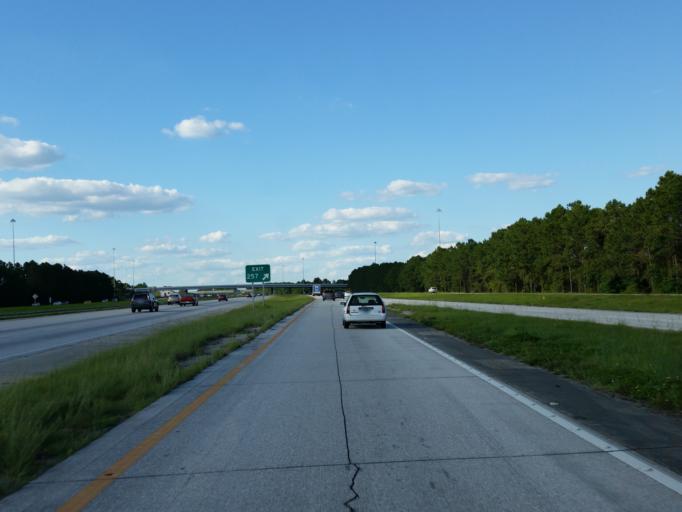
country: US
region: Florida
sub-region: Hillsborough County
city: Progress Village
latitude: 27.9174
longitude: -82.3358
